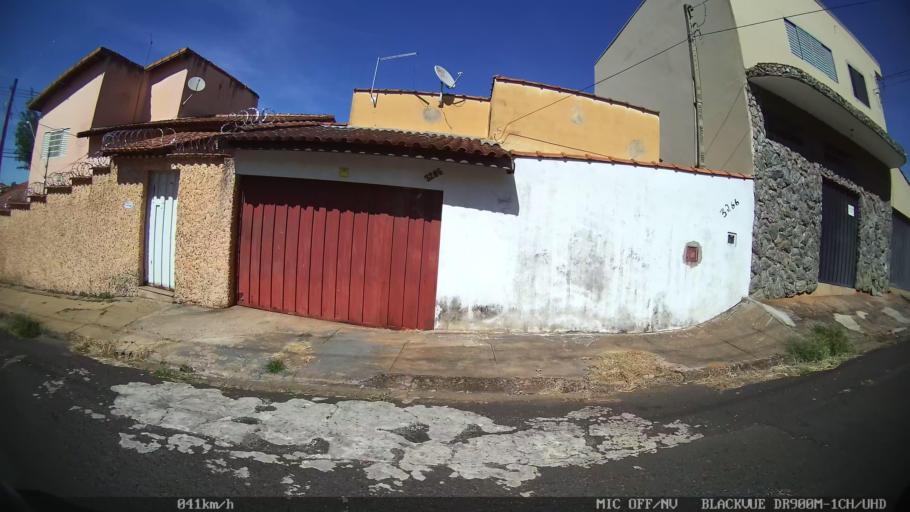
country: BR
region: Sao Paulo
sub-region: Franca
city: Franca
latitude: -20.5471
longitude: -47.3803
